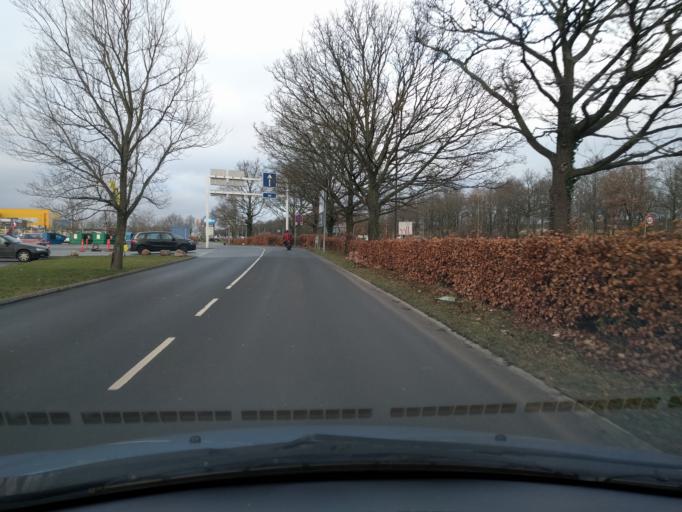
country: DK
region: South Denmark
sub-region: Odense Kommune
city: Neder Holluf
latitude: 55.3778
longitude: 10.4348
